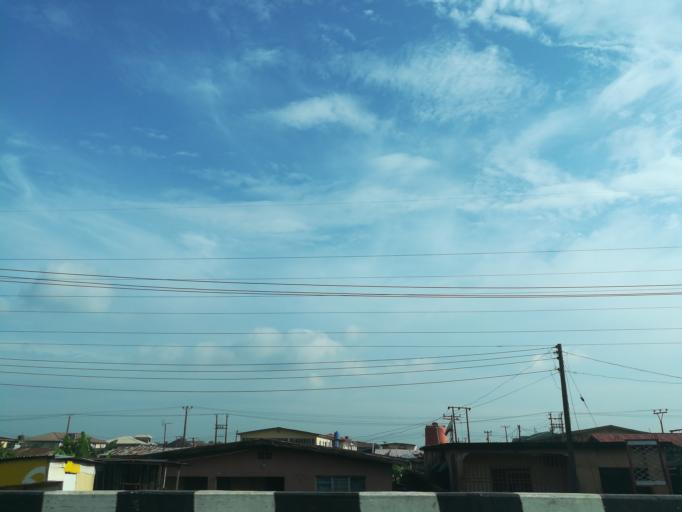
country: NG
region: Lagos
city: Ojota
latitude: 6.6087
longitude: 3.4251
